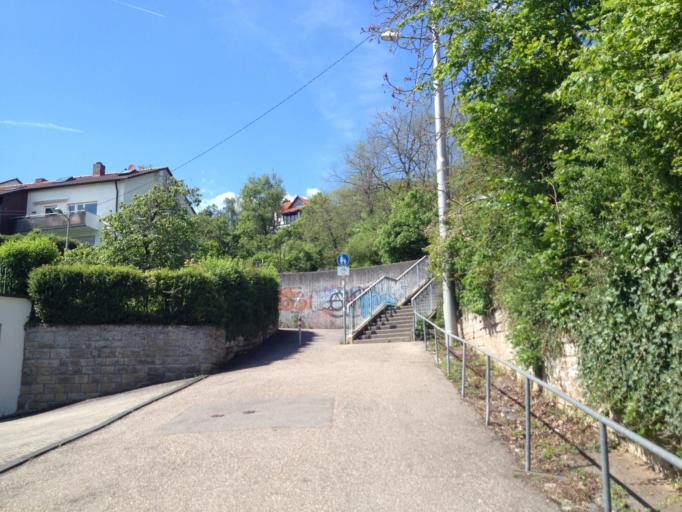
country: DE
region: Baden-Wuerttemberg
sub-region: Regierungsbezirk Stuttgart
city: Stuttgart Feuerbach
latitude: 48.7802
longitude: 9.1201
